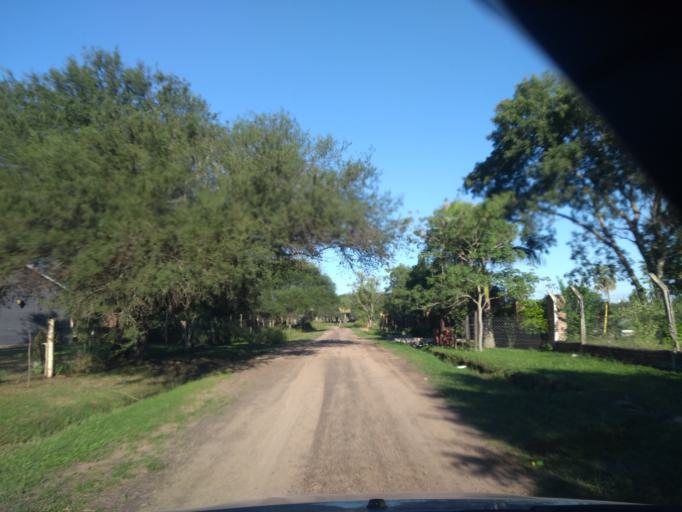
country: AR
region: Chaco
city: Barranqueras
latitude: -27.4410
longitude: -58.9055
